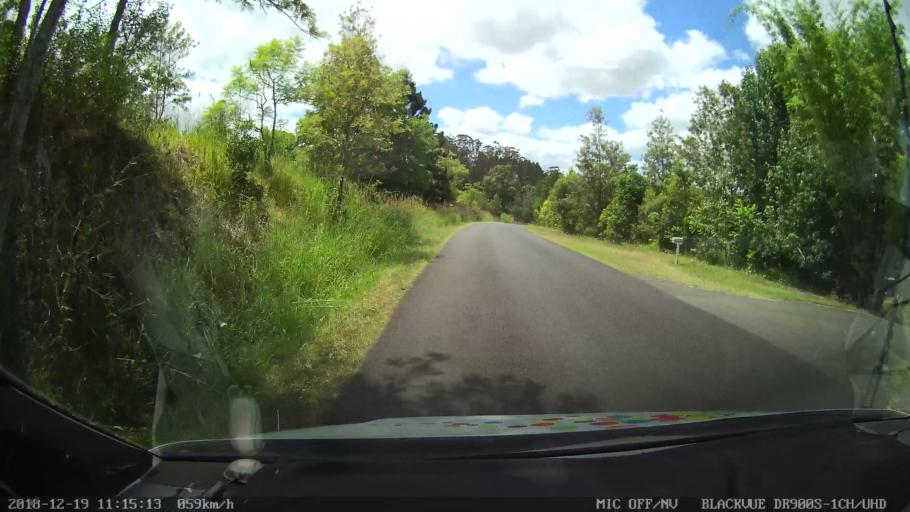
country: AU
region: New South Wales
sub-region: Lismore Municipality
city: Nimbin
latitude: -28.6661
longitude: 153.2769
